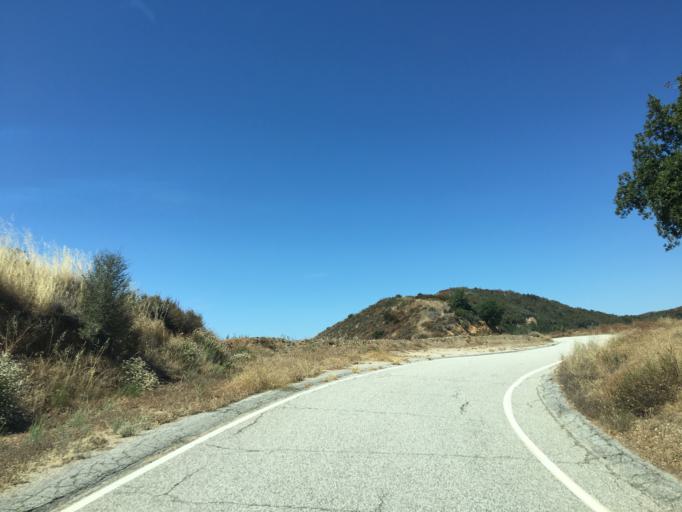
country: US
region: California
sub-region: Los Angeles County
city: San Dimas
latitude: 34.2079
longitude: -117.7833
